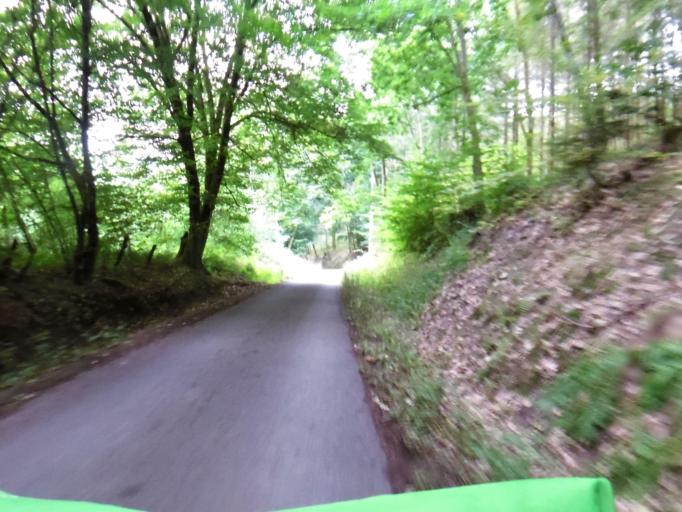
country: BE
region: Wallonia
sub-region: Province de Namur
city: Bievre
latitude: 49.8708
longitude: 4.9914
